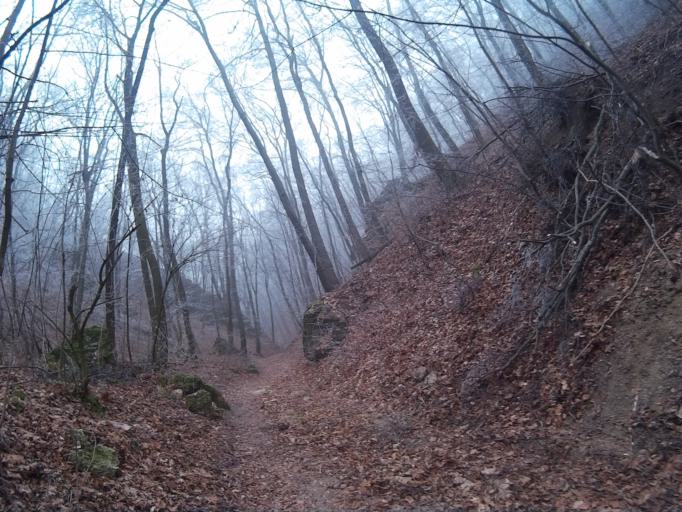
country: HU
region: Fejer
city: Bodajk
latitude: 47.3627
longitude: 18.2750
